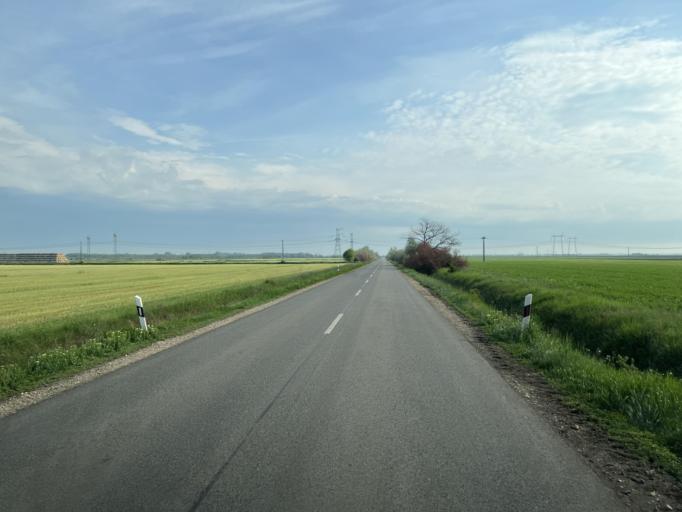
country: HU
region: Pest
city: Cegled
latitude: 47.2294
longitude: 19.7727
